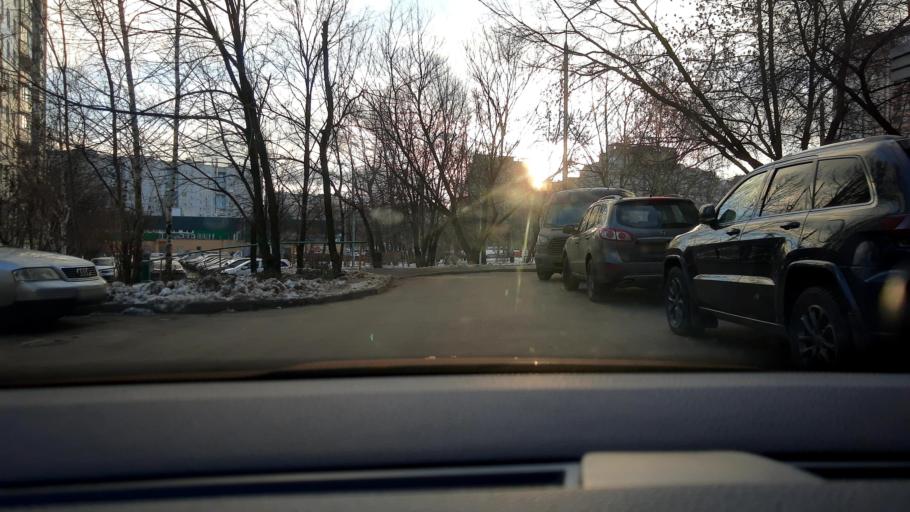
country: RU
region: Moskovskaya
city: Vostochnoe Degunino
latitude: 55.8793
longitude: 37.5593
